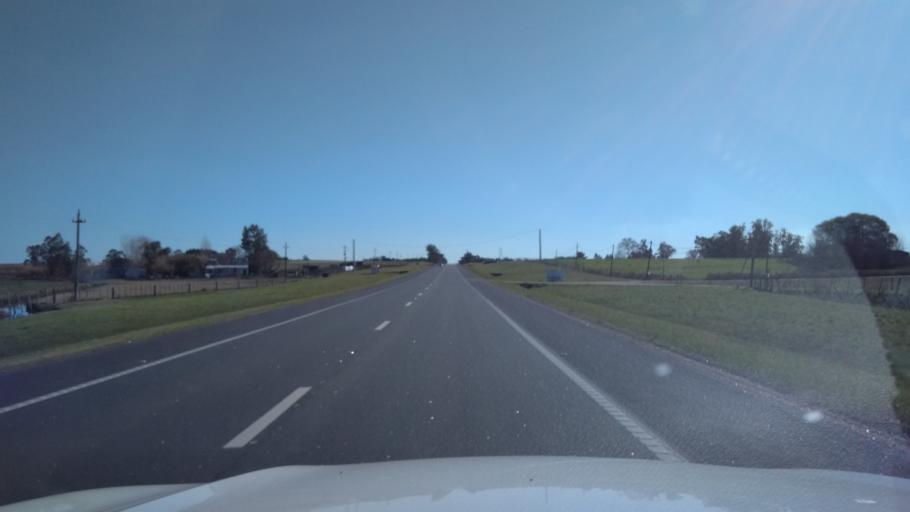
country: UY
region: Canelones
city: San Jacinto
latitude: -34.5266
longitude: -55.9609
